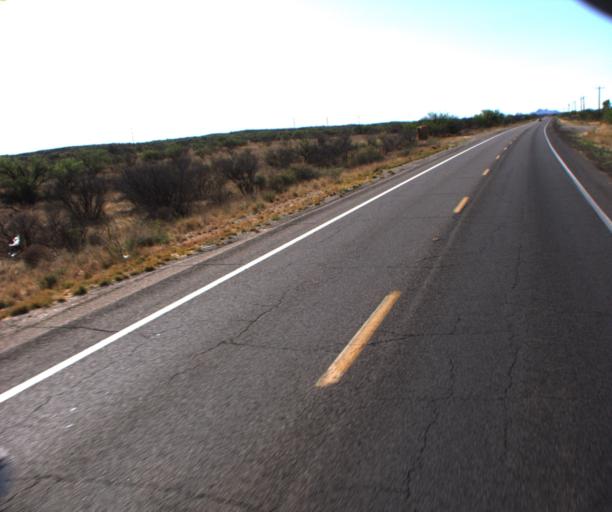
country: US
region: Arizona
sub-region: Cochise County
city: Saint David
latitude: 31.8611
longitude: -110.2042
